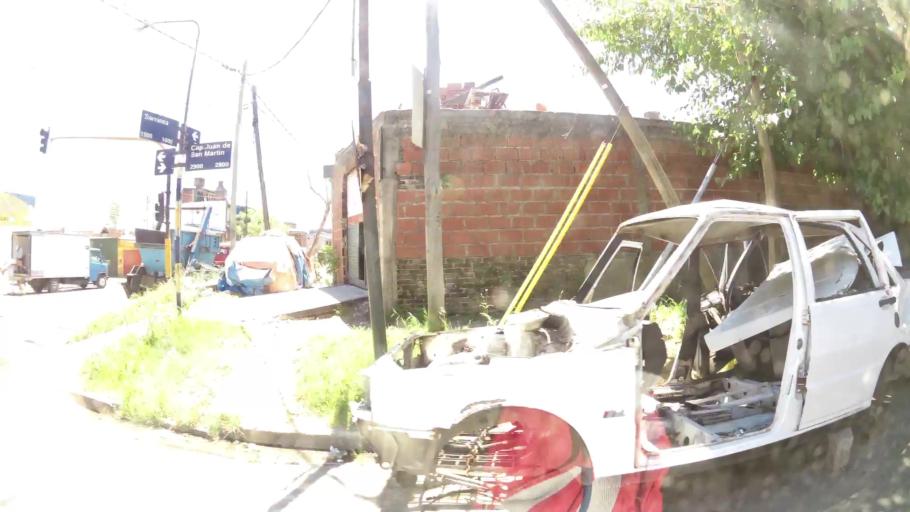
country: AR
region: Buenos Aires
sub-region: Partido de Tigre
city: Tigre
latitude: -34.5038
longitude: -58.5844
